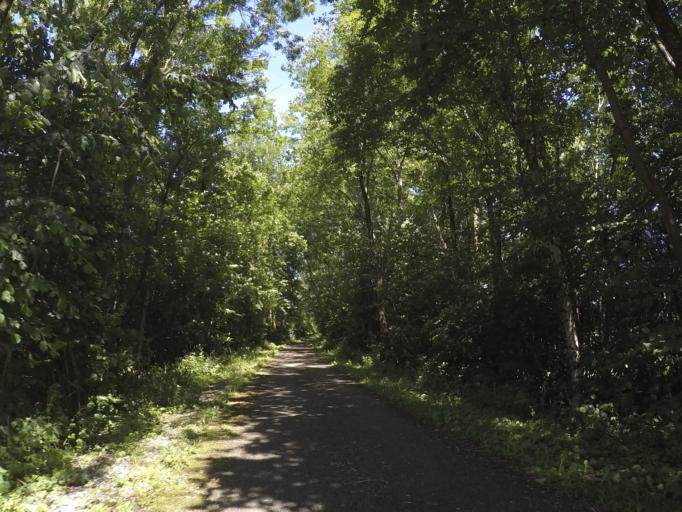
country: BE
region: Wallonia
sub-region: Province de Namur
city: Hamois
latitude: 50.3528
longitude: 5.1754
